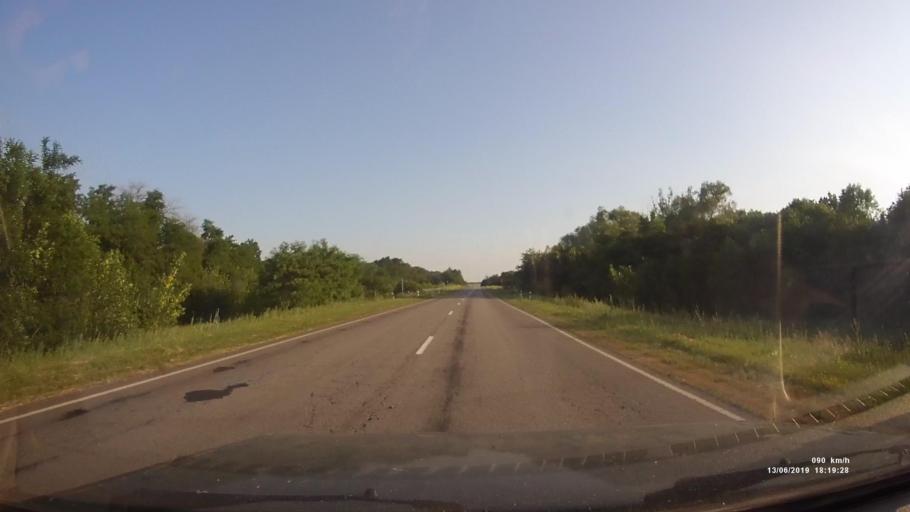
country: RU
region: Rostov
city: Kazanskaya
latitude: 49.8955
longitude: 41.3062
